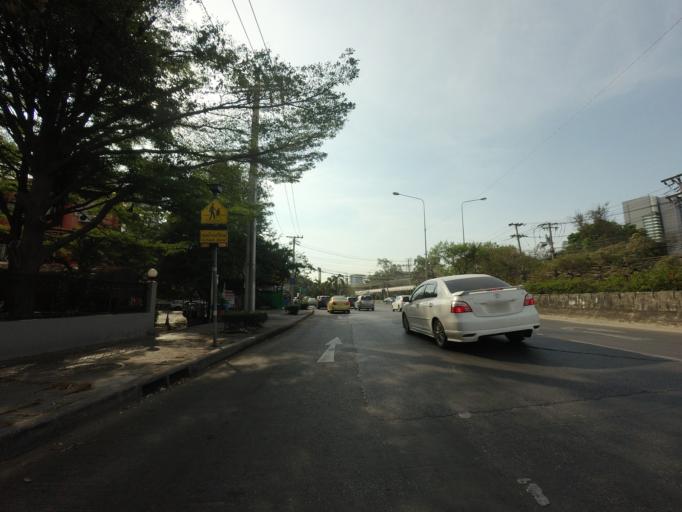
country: TH
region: Bangkok
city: Bang Kapi
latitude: 13.7553
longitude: 100.6284
